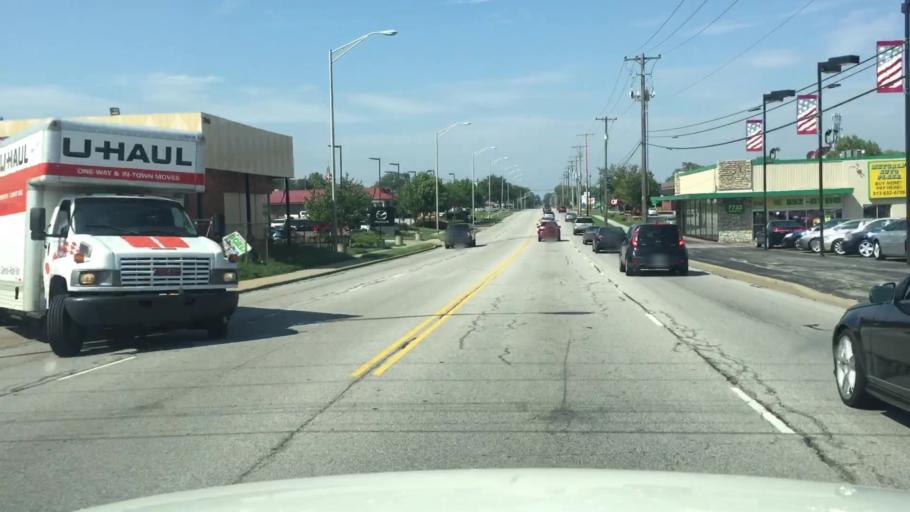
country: US
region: Kansas
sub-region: Johnson County
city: Overland Park
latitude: 38.9877
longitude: -94.6677
